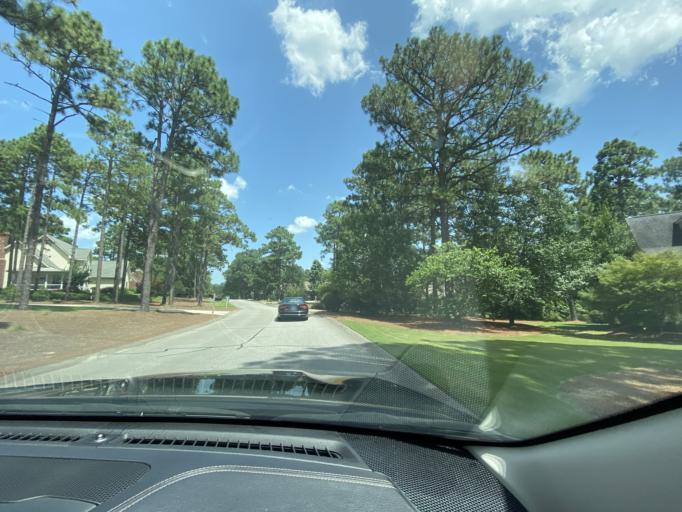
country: US
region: North Carolina
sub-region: Moore County
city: Pinehurst
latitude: 35.1974
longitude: -79.4375
